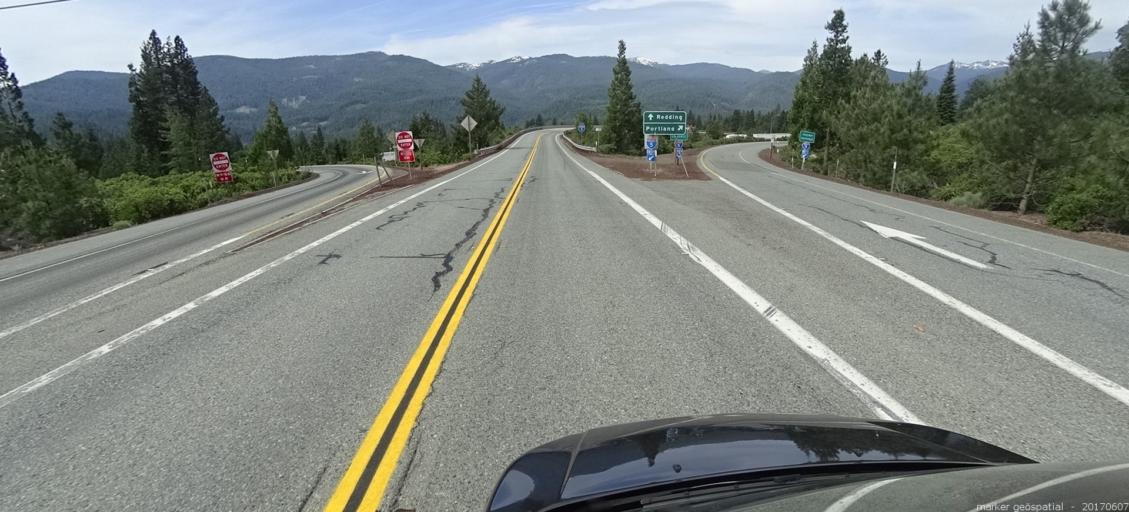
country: US
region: California
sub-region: Siskiyou County
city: Mount Shasta
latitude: 41.2863
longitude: -122.2999
